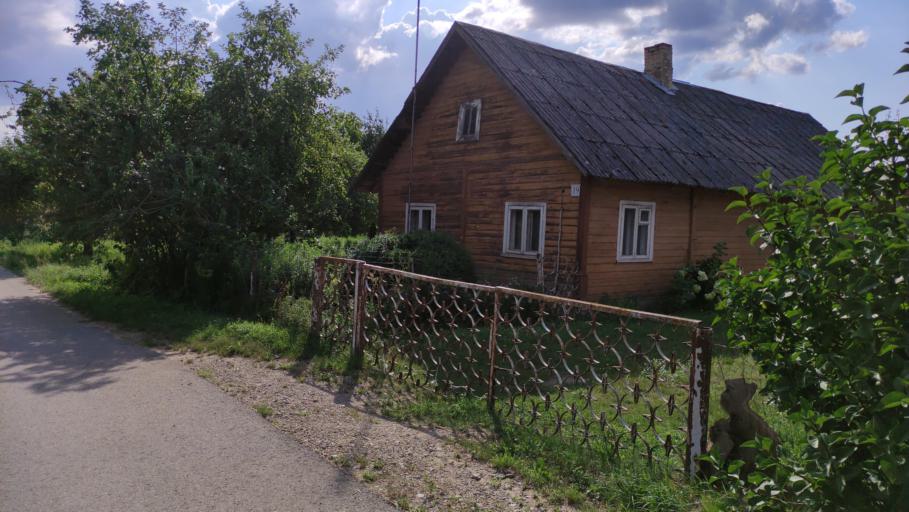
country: LT
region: Alytaus apskritis
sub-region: Alytus
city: Alytus
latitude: 54.4339
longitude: 24.0718
